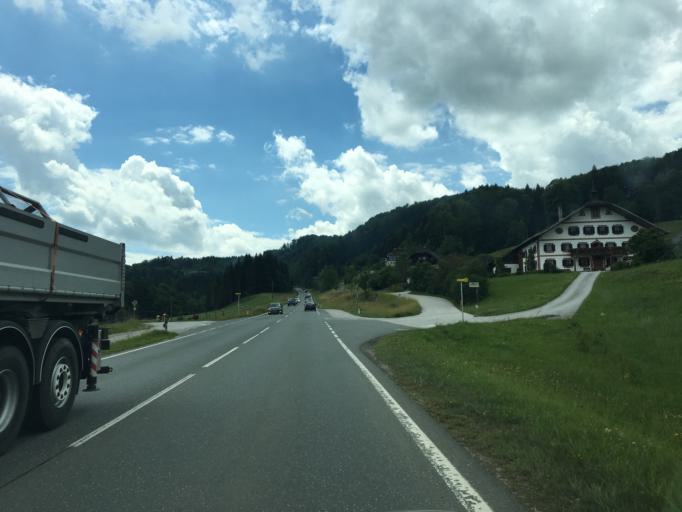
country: AT
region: Salzburg
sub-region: Politischer Bezirk Salzburg-Umgebung
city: Hof bei Salzburg
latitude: 47.8410
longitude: 13.2077
